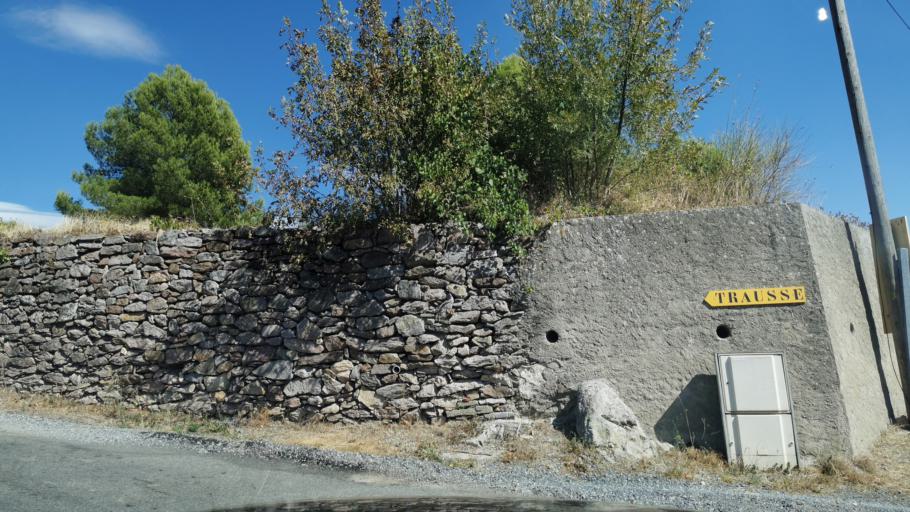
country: FR
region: Languedoc-Roussillon
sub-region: Departement de l'Aude
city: Caunes-Minervois
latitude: 43.3249
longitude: 2.5307
